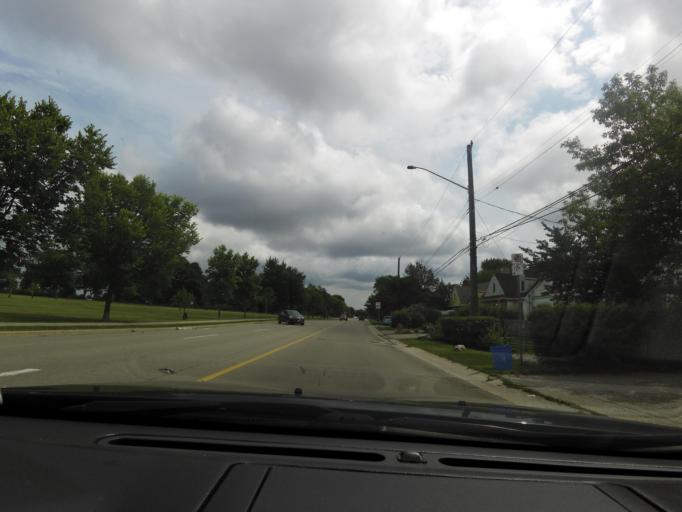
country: CA
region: Ontario
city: Hamilton
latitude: 43.2368
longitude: -79.8349
